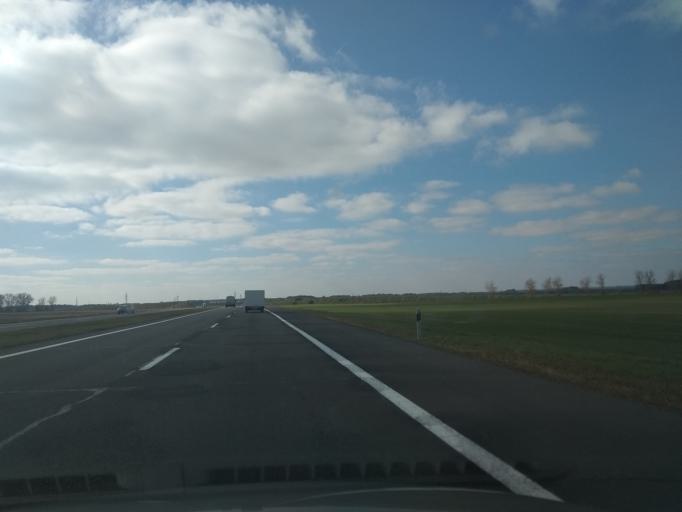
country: BY
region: Brest
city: Haradzishcha
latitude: 53.2383
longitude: 26.1846
